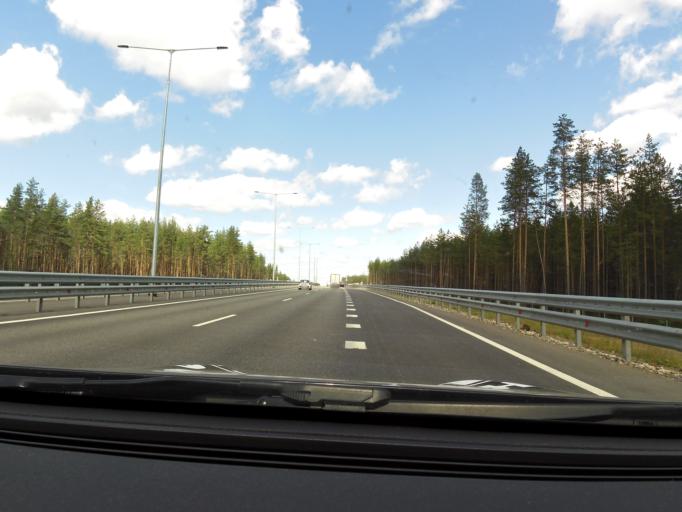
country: RU
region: Tverskaya
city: Krasnomayskiy
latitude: 57.6764
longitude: 34.2267
